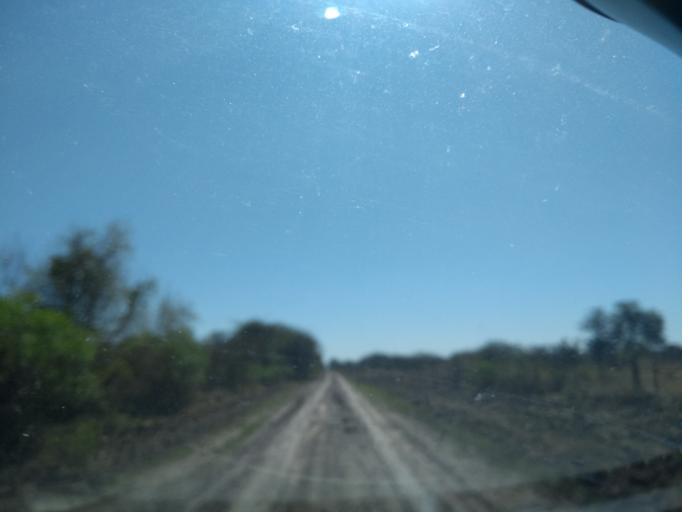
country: AR
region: Chaco
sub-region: Departamento de Quitilipi
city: Quitilipi
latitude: -26.7356
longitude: -60.2339
